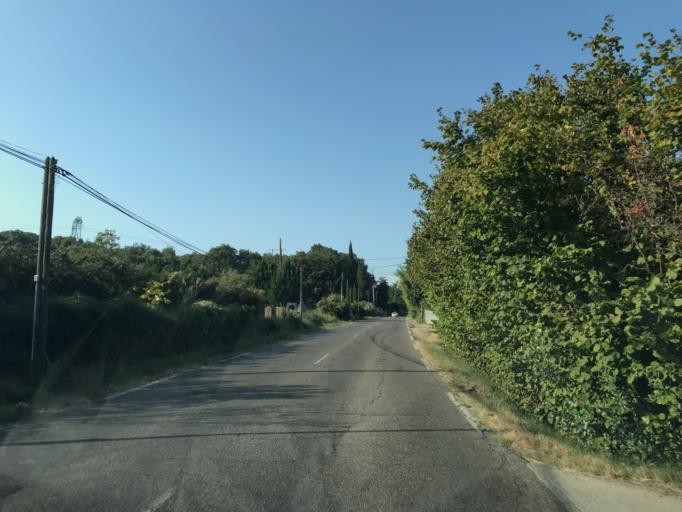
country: FR
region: Provence-Alpes-Cote d'Azur
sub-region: Departement des Bouches-du-Rhone
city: Saint-Chamas
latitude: 43.5645
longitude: 5.0156
